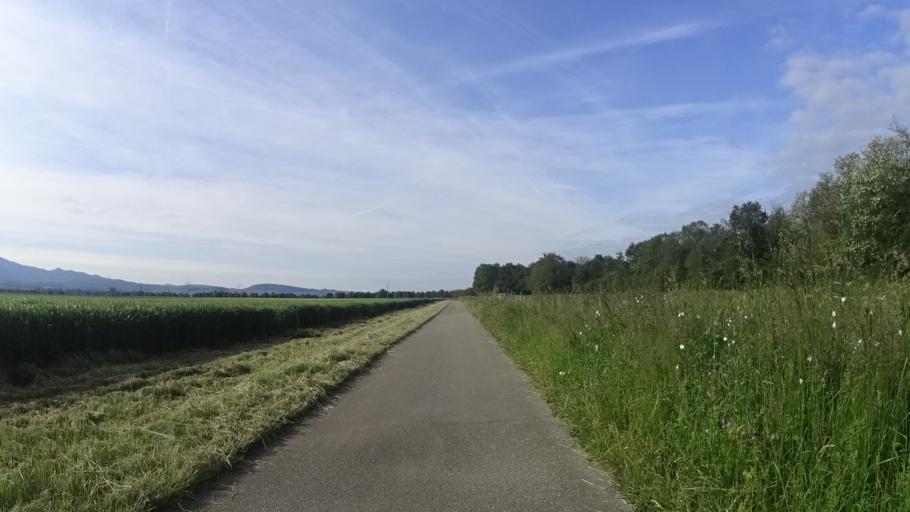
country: DE
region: Baden-Wuerttemberg
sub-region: Freiburg Region
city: Neuenburg am Rhein
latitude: 47.8523
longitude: 7.5838
